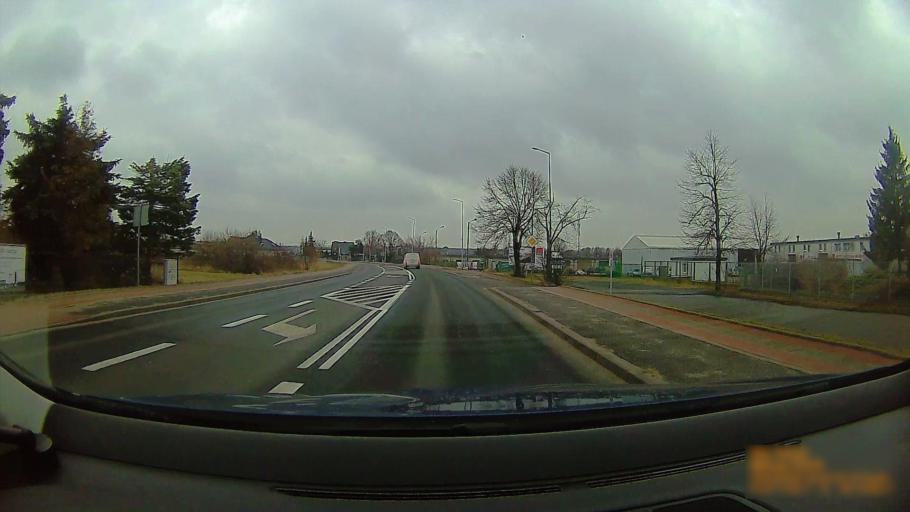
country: PL
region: Greater Poland Voivodeship
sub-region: Konin
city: Konin
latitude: 52.1972
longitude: 18.2612
